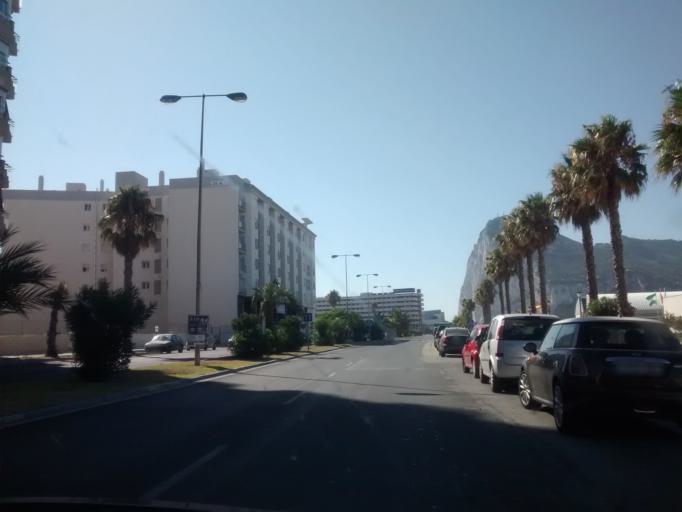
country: ES
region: Andalusia
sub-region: Provincia de Cadiz
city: La Linea de la Concepcion
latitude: 36.1616
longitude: -5.3564
